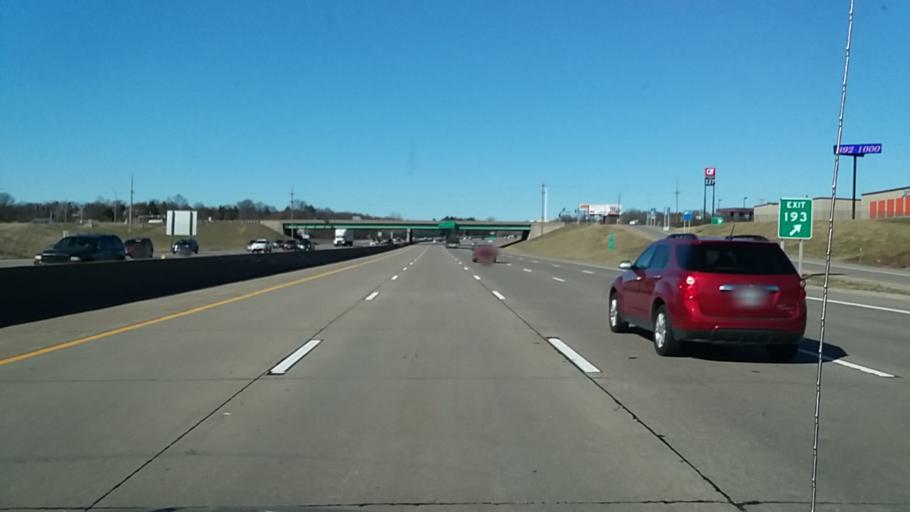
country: US
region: Missouri
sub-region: Jefferson County
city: Arnold
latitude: 38.4593
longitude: -90.3745
